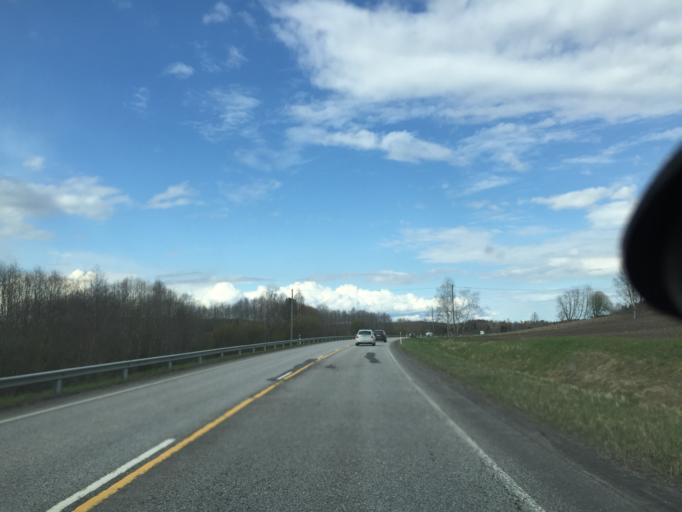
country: FI
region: Uusimaa
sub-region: Helsinki
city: Lohja
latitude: 60.1949
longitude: 24.0101
